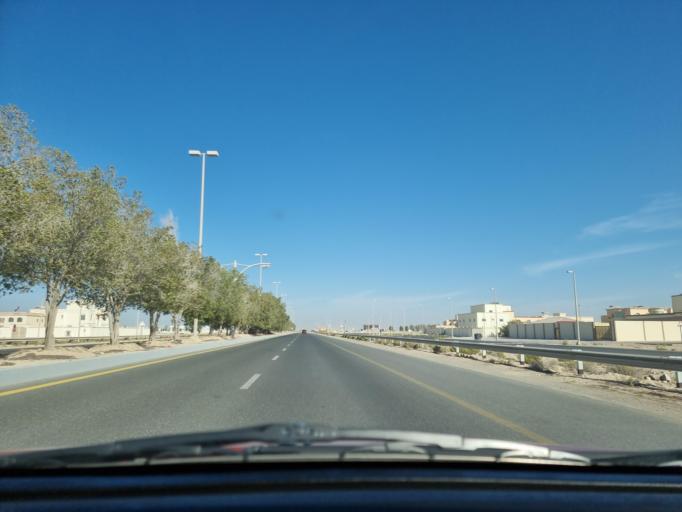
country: AE
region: Abu Dhabi
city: Abu Dhabi
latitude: 24.3942
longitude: 54.6942
